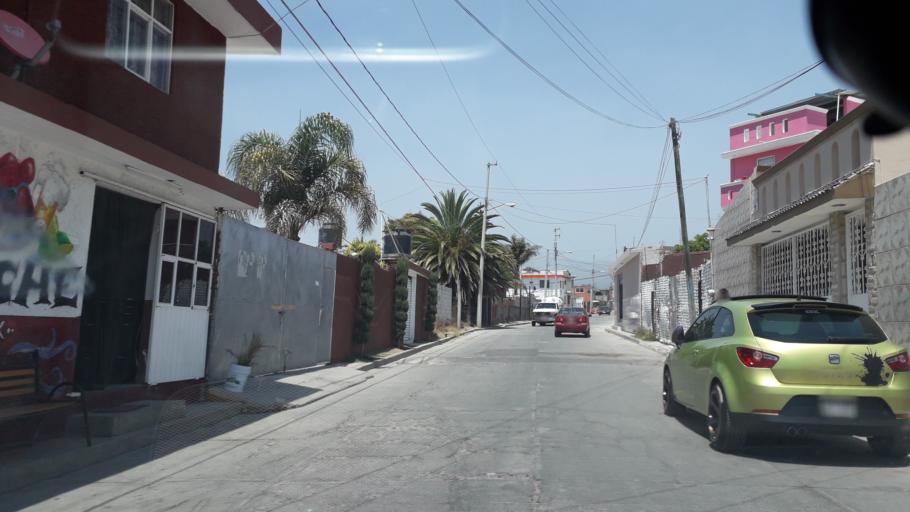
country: MX
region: Puebla
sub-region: Puebla
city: Santa Maria Xonacatepec
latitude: 19.0835
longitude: -98.1099
